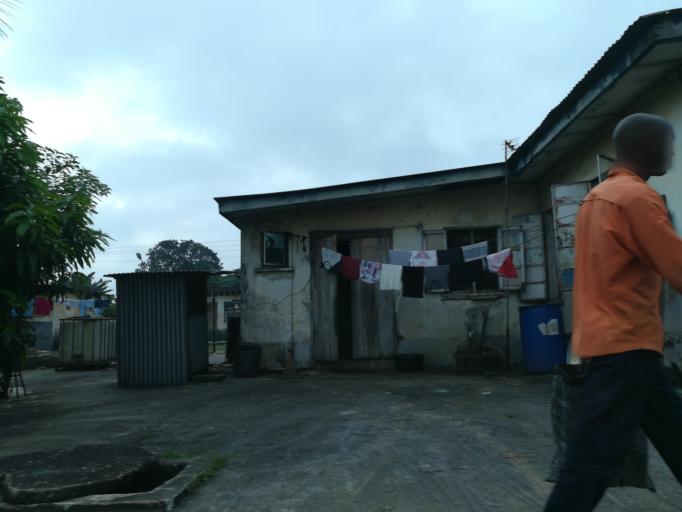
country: NG
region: Rivers
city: Port Harcourt
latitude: 4.7585
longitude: 7.0149
